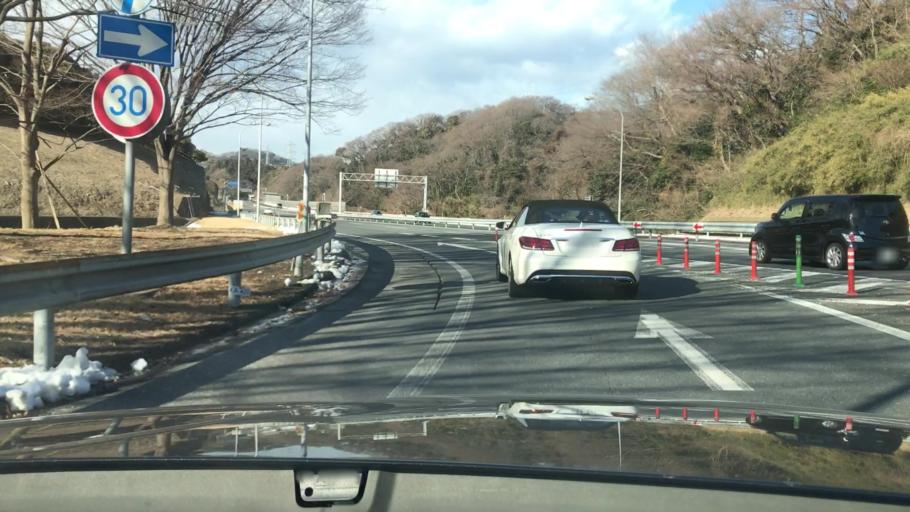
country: JP
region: Kanagawa
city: Zushi
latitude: 35.2926
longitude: 139.6189
